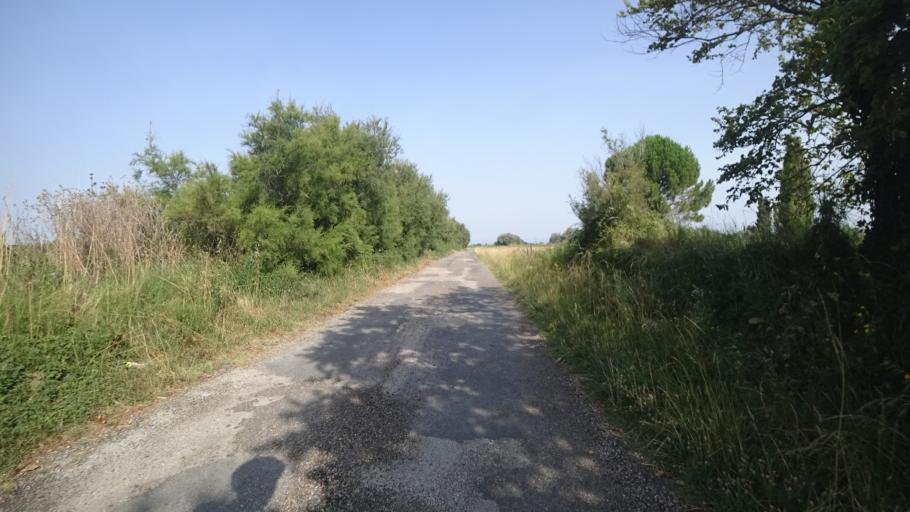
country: FR
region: Languedoc-Roussillon
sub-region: Departement des Pyrenees-Orientales
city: Sainte-Marie-Plage
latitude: 42.7320
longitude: 3.0117
